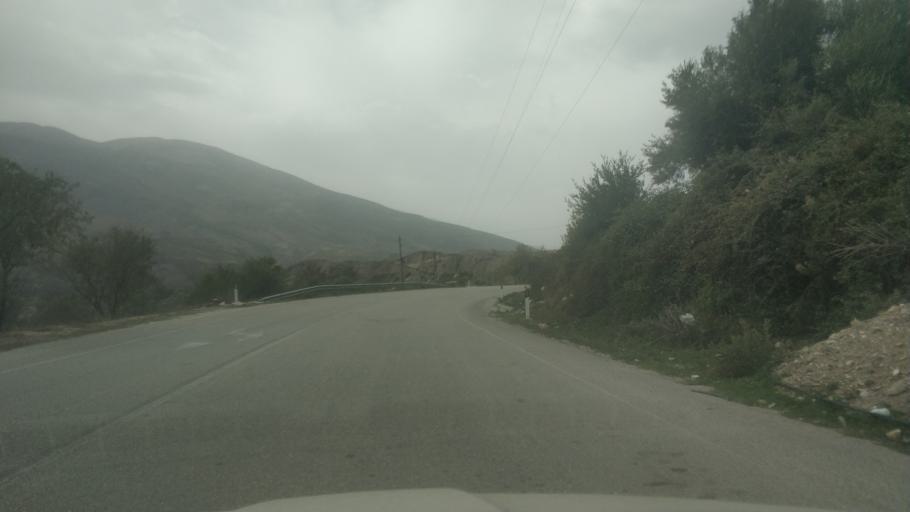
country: AL
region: Gjirokaster
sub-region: Rrethi i Tepelenes
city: Memaliaj
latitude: 40.3533
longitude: 19.9522
